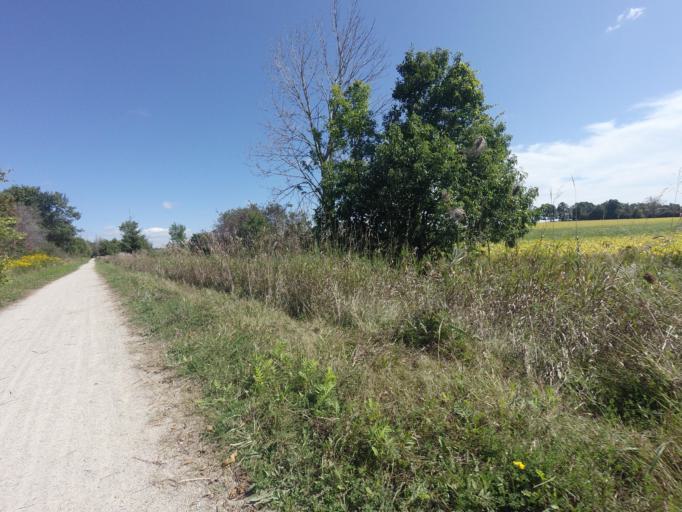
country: CA
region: Ontario
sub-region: Wellington County
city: Guelph
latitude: 43.7311
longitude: -80.3689
